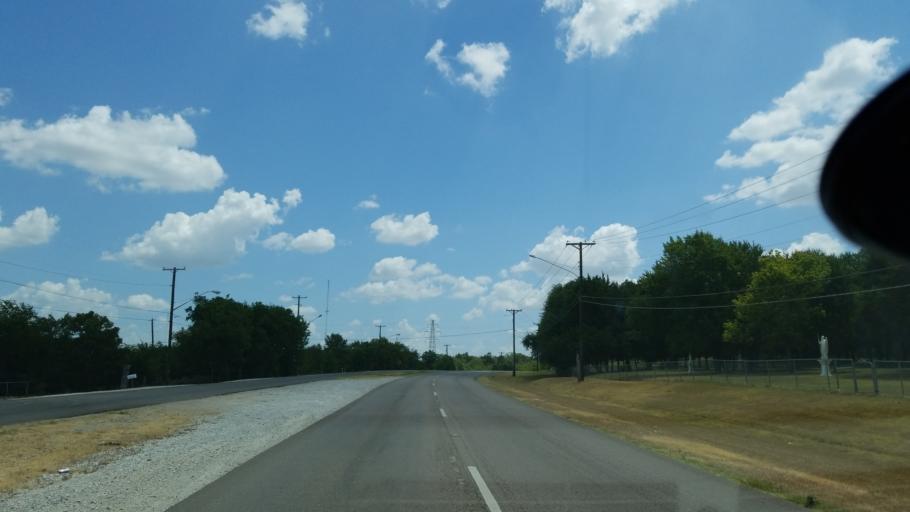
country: US
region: Texas
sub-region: Dallas County
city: Cockrell Hill
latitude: 32.7437
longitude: -96.9054
